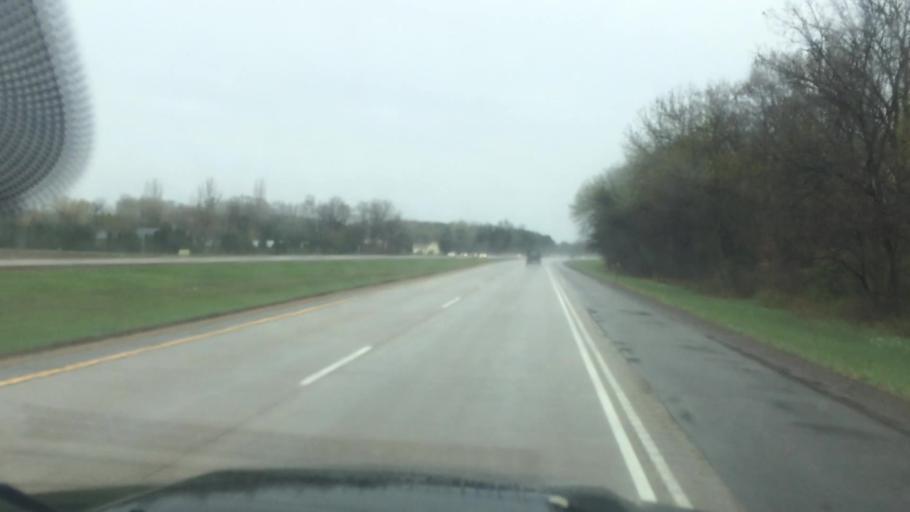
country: US
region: Wisconsin
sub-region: Portage County
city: Stevens Point
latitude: 44.6468
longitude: -89.6373
